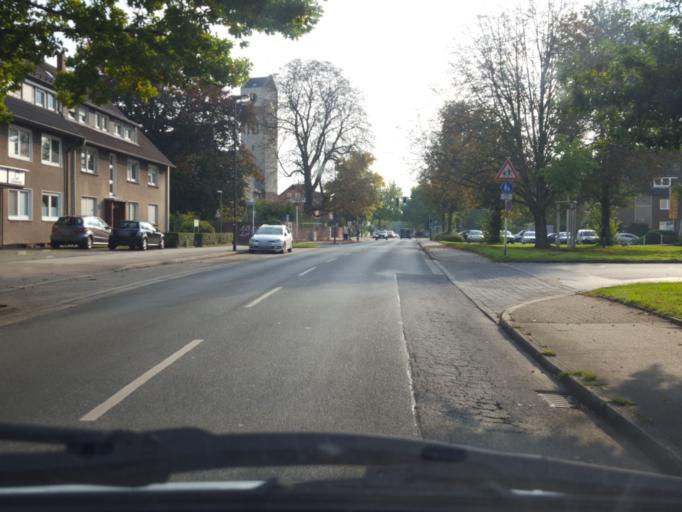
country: DE
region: North Rhine-Westphalia
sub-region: Regierungsbezirk Dusseldorf
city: Essen
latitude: 51.4186
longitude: 6.9581
